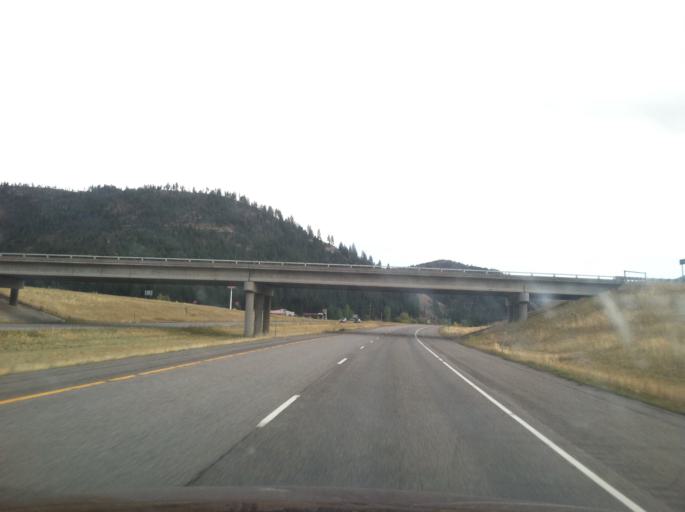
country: US
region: Montana
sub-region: Missoula County
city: Clinton
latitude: 46.7815
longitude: -113.7142
